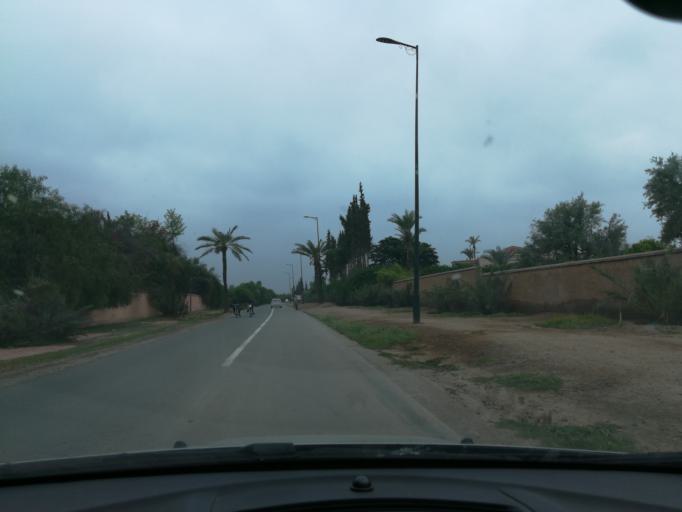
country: MA
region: Marrakech-Tensift-Al Haouz
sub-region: Marrakech
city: Marrakesh
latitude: 31.6510
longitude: -7.9738
